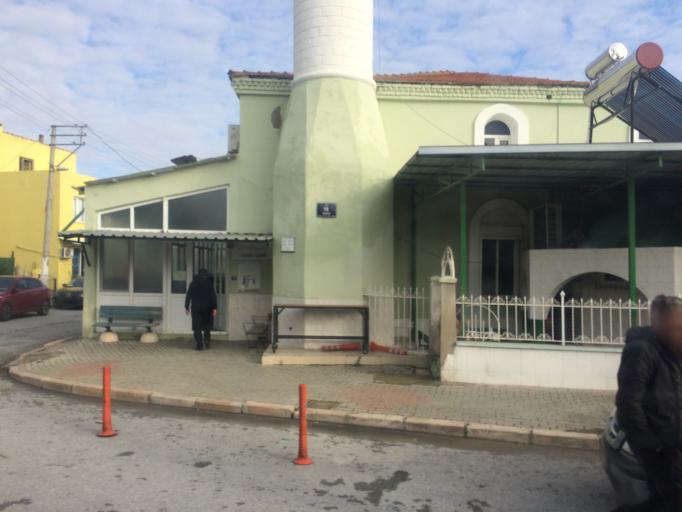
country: TR
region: Izmir
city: Karsiyaka
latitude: 38.4943
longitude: 26.9518
